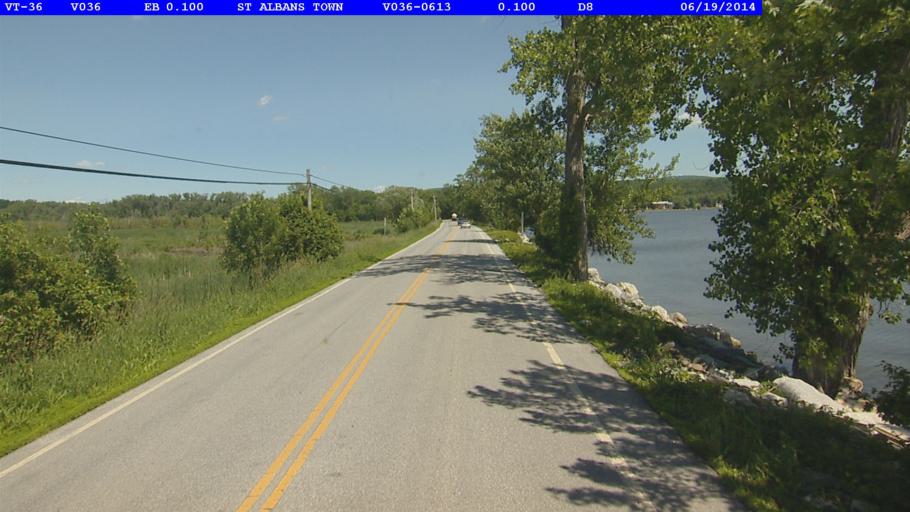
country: US
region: Vermont
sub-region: Franklin County
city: Saint Albans
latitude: 44.8104
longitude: -73.1495
